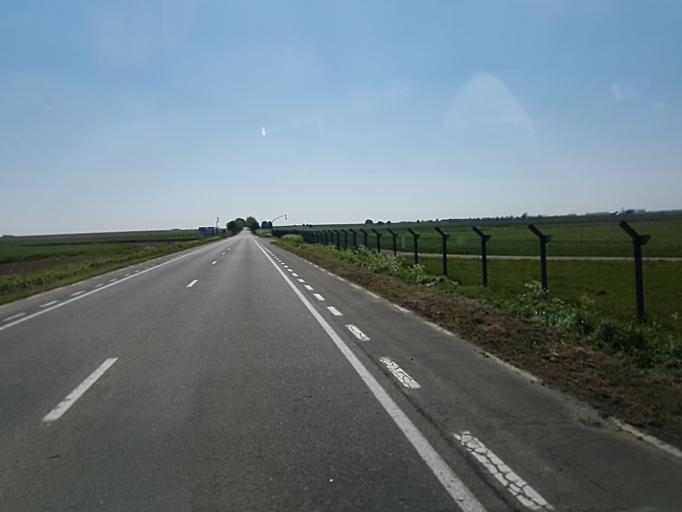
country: BE
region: Wallonia
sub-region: Province du Hainaut
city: Brugelette
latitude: 50.5793
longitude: 3.8601
